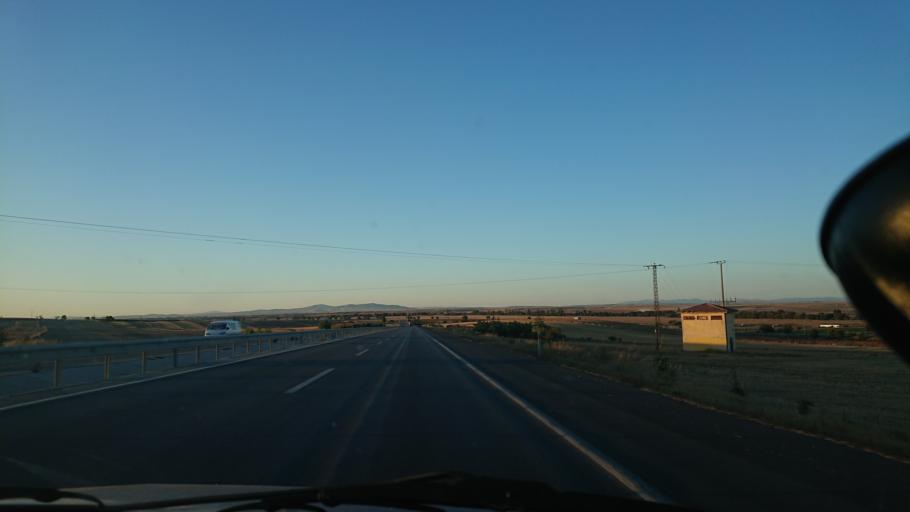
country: TR
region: Eskisehir
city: Mahmudiye
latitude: 39.5107
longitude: 30.9647
